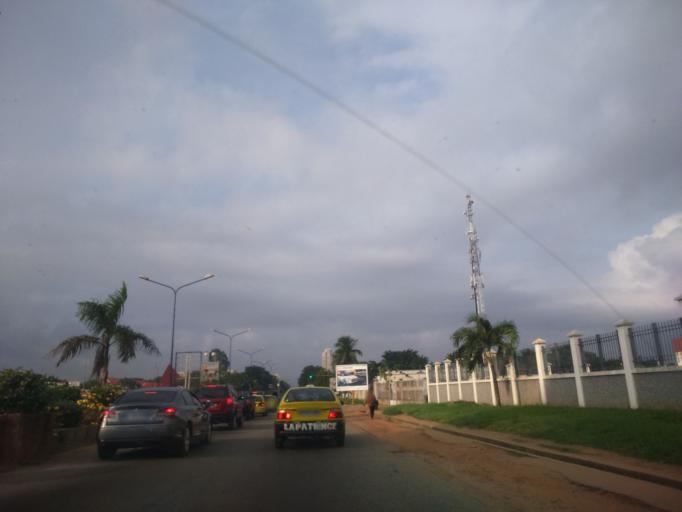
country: CI
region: Lagunes
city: Abidjan
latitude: 5.3376
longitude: -4.0038
